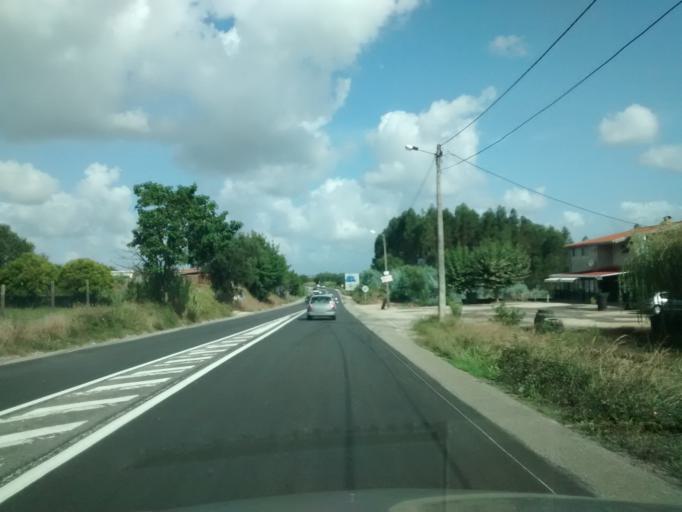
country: PT
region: Aveiro
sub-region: Oliveira do Bairro
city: Oia
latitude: 40.5442
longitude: -8.5340
